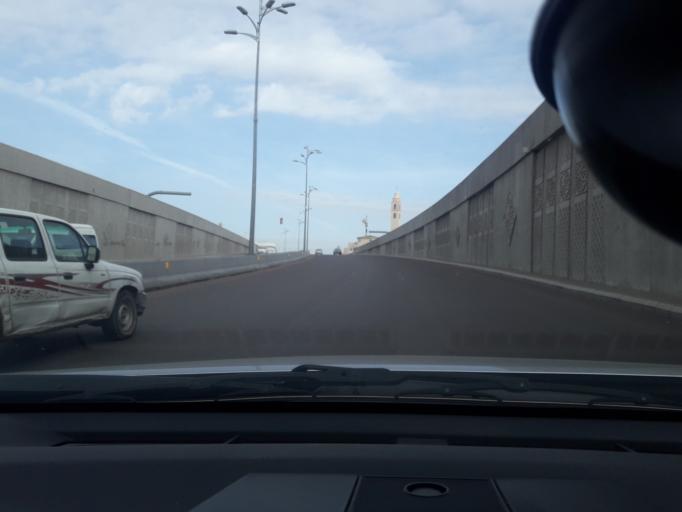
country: SA
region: Al Madinah al Munawwarah
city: Medina
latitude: 24.4696
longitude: 39.6194
